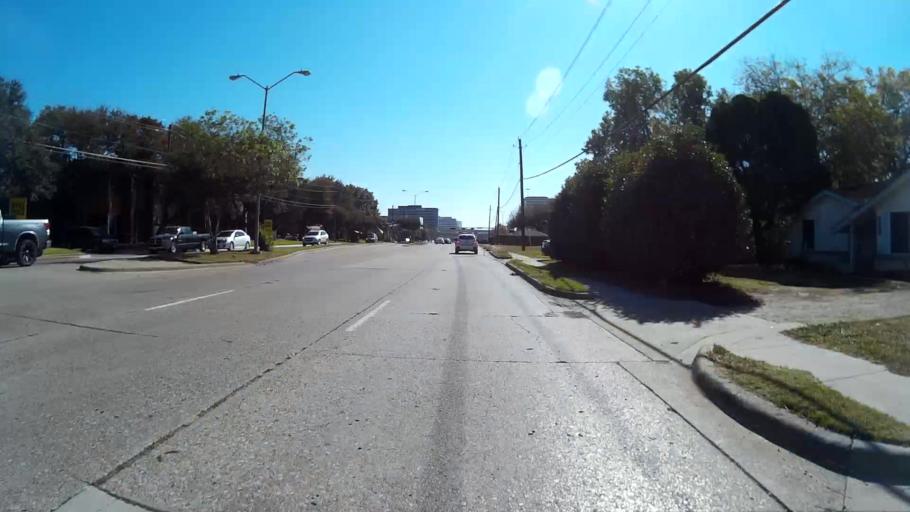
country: US
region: Texas
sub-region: Dallas County
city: Richardson
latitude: 32.9284
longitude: -96.7691
